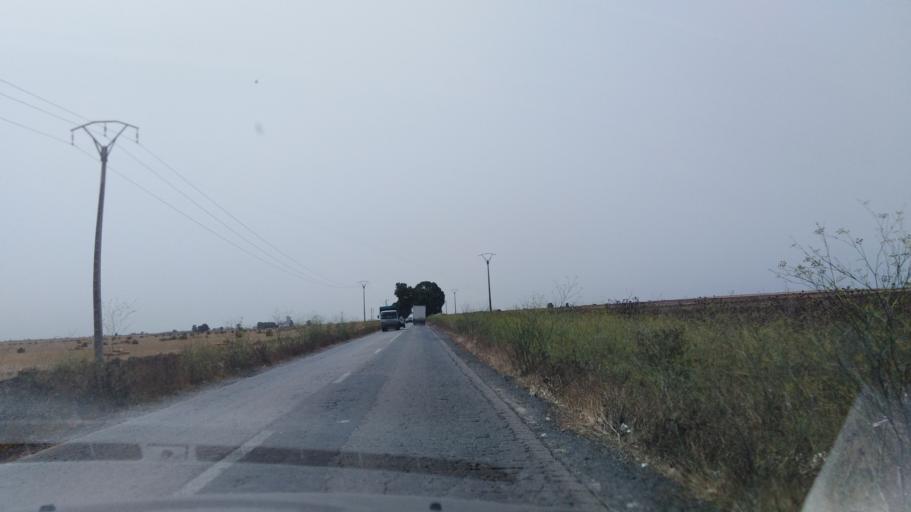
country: MA
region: Grand Casablanca
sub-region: Nouaceur
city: Dar Bouazza
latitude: 33.4097
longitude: -7.8082
